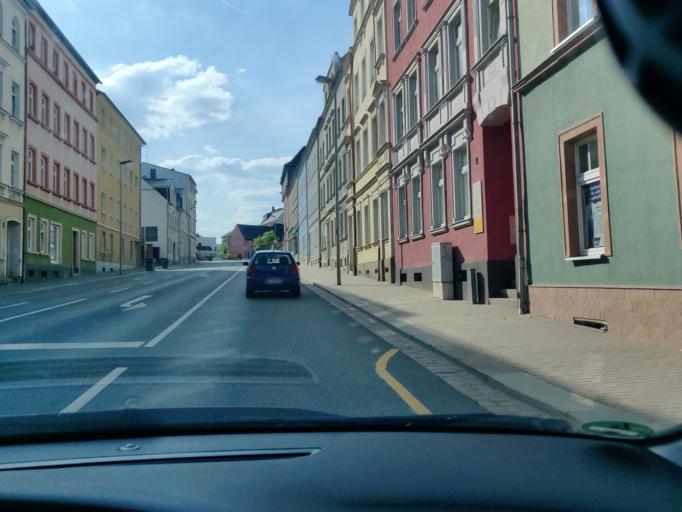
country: DE
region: Saxony
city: Mittweida
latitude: 50.9869
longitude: 12.9755
